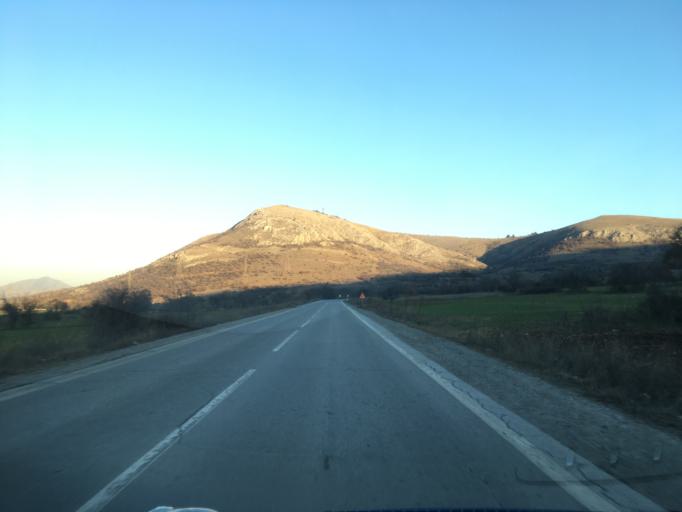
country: GR
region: West Macedonia
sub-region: Nomos Kozanis
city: Kozani
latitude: 40.3167
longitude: 21.7537
